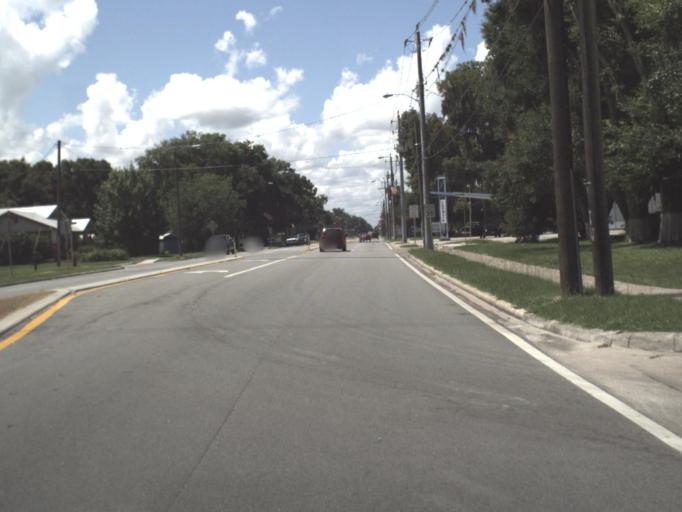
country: US
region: Florida
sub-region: Putnam County
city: Crescent City
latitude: 29.4371
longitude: -81.5106
